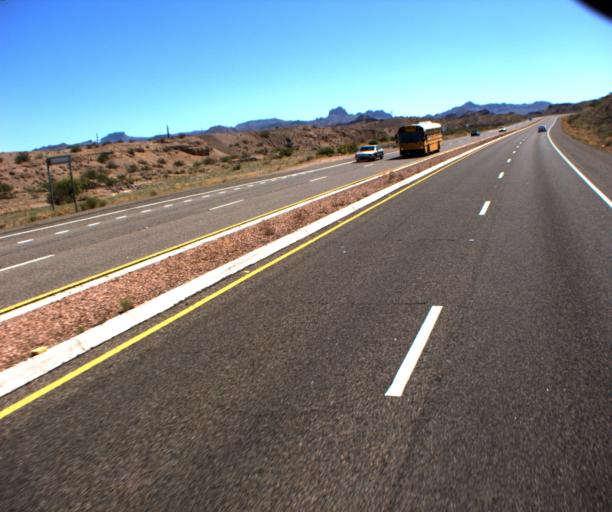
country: US
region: Nevada
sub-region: Clark County
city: Laughlin
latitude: 35.1908
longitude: -114.5247
